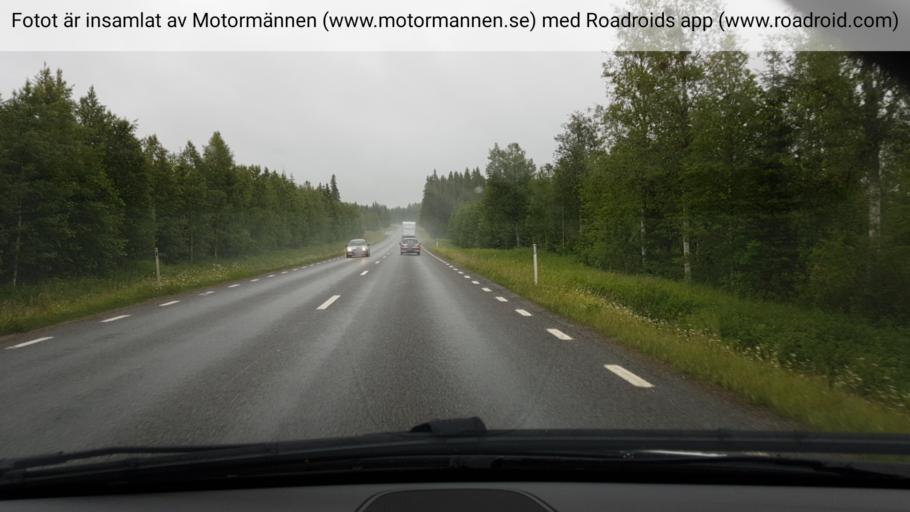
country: SE
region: Jaemtland
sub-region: OEstersunds Kommun
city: Lit
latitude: 63.4809
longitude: 15.2251
